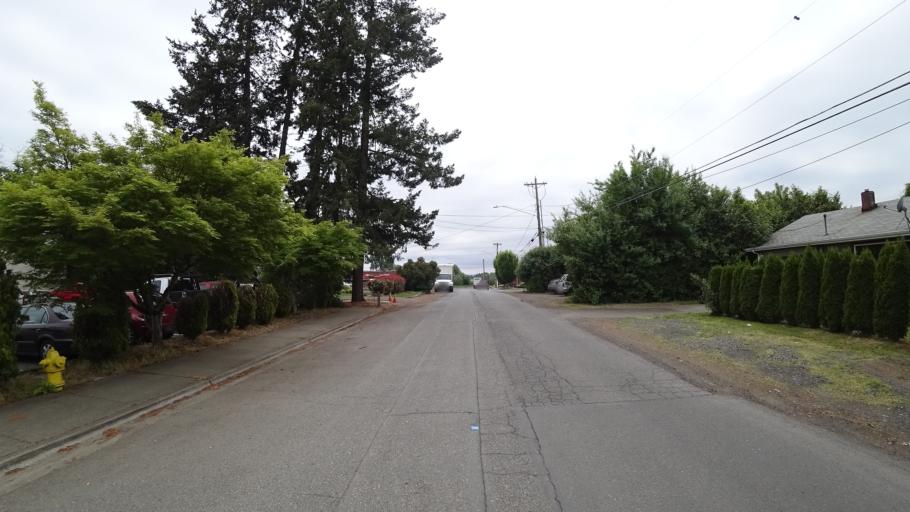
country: US
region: Oregon
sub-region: Washington County
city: Aloha
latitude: 45.4991
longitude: -122.9048
